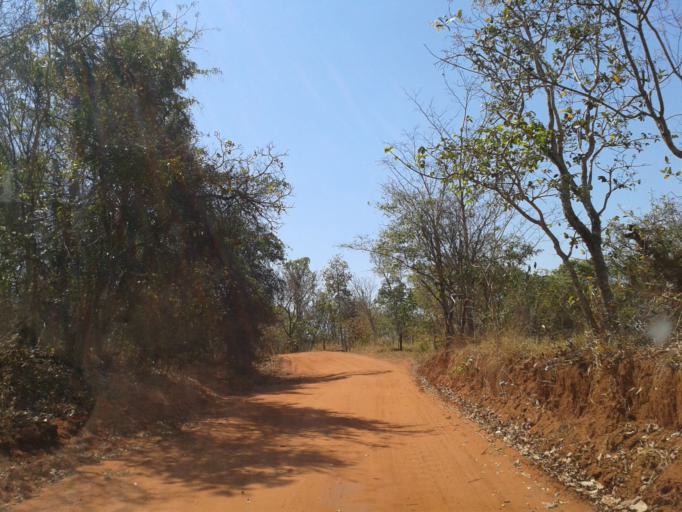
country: BR
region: Minas Gerais
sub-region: Ituiutaba
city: Ituiutaba
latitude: -19.0914
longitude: -49.2971
